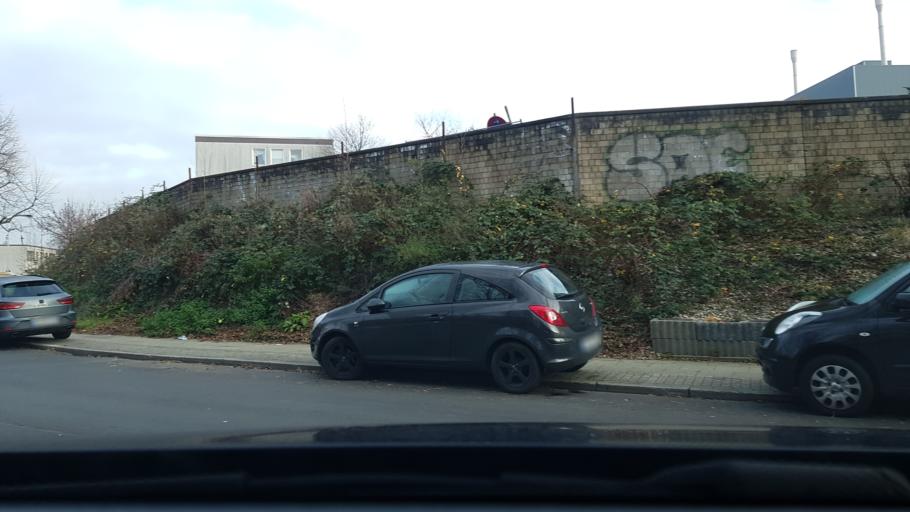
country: DE
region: North Rhine-Westphalia
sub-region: Regierungsbezirk Dusseldorf
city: Muelheim (Ruhr)
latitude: 51.4379
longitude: 6.9169
